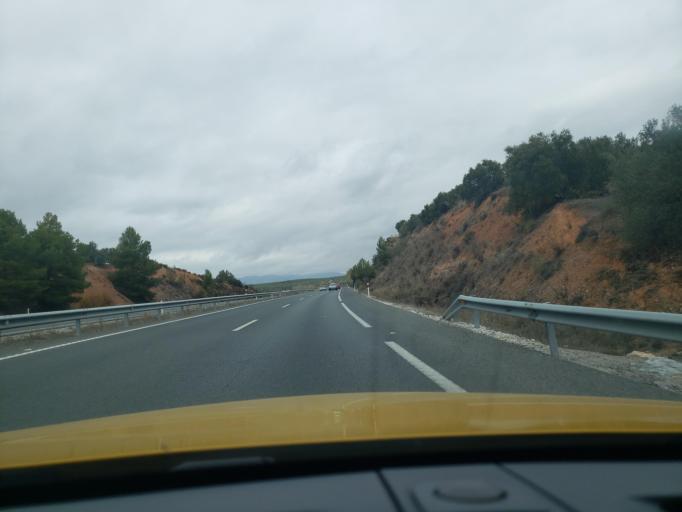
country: ES
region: Andalusia
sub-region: Provincia de Granada
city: Calicasas
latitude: 37.2890
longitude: -3.6580
